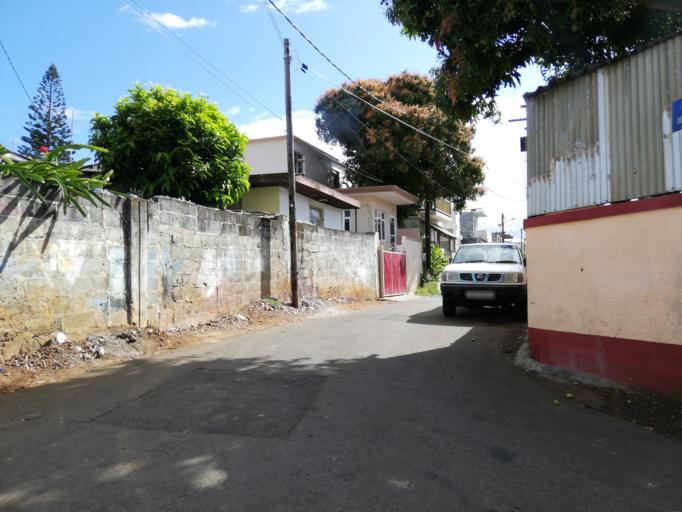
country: MU
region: Black River
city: Petite Riviere
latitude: -20.2235
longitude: 57.4557
